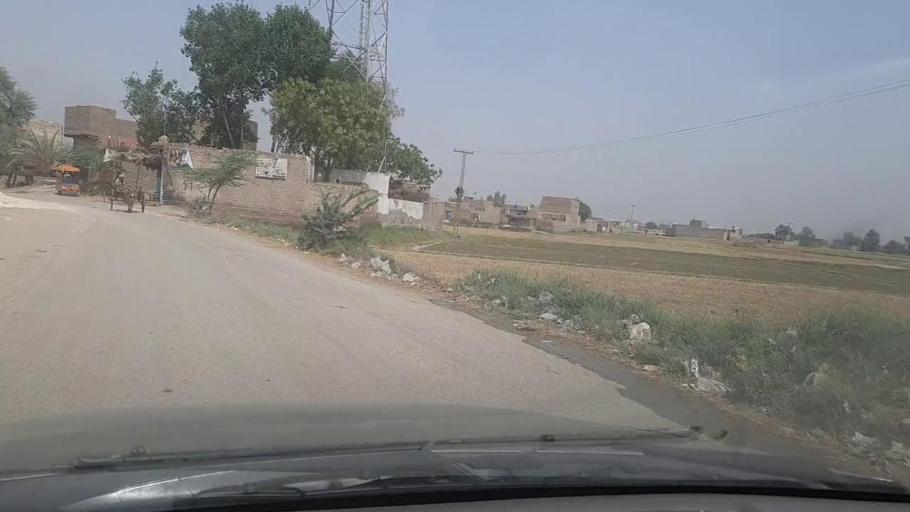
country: PK
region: Sindh
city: Madeji
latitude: 27.7992
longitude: 68.4073
